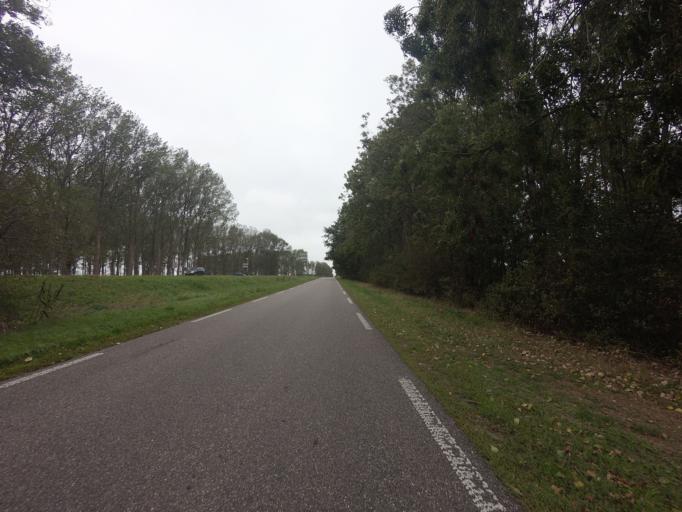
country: NL
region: Friesland
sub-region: Gemeente Opsterland
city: Tijnje
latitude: 53.0208
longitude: 6.0138
